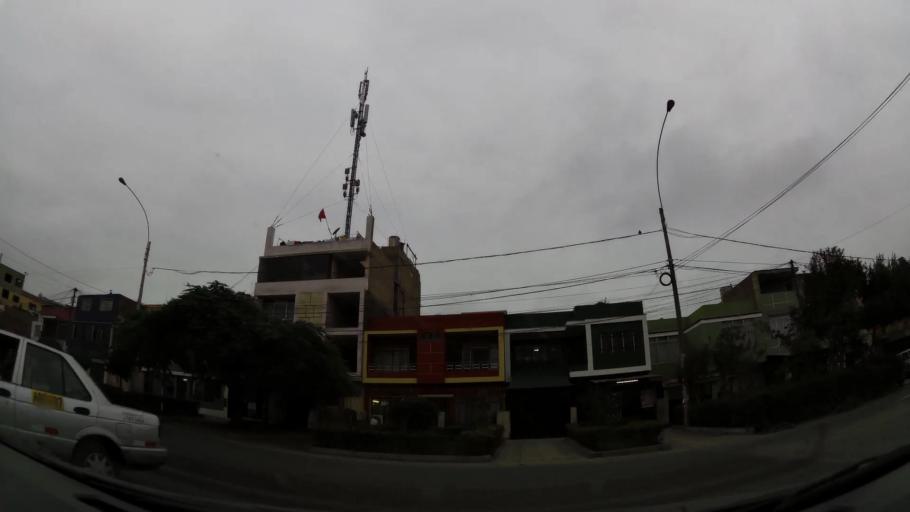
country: PE
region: Lima
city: Lima
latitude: -12.0547
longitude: -77.0708
